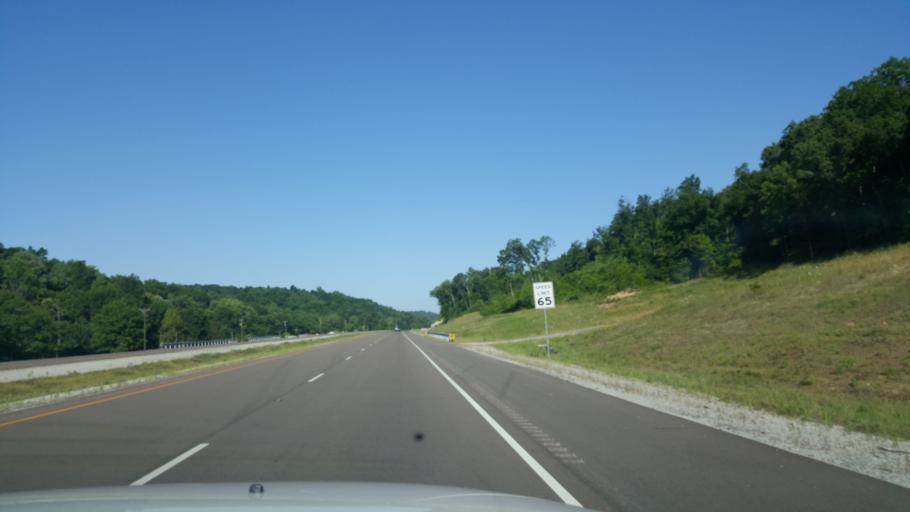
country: US
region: Tennessee
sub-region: Wayne County
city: Waynesboro
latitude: 35.2962
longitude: -87.8224
